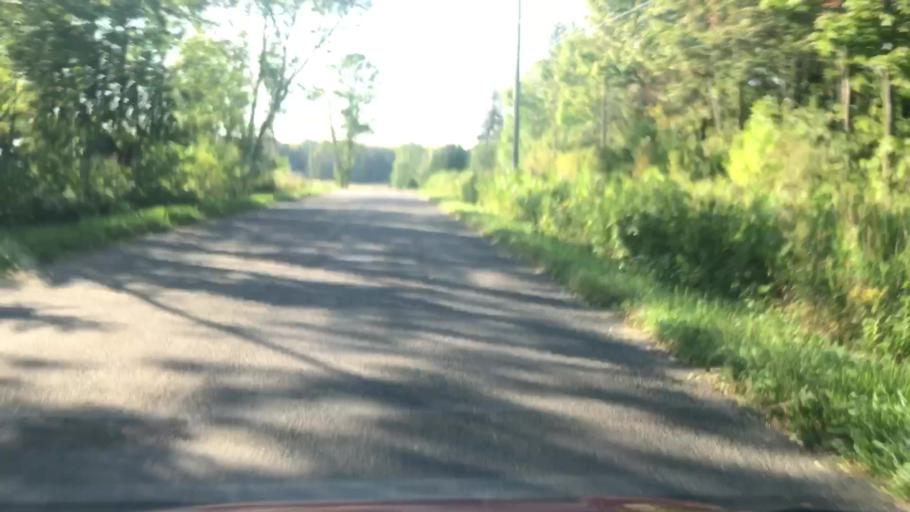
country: US
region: Michigan
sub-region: Chippewa County
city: Sault Ste. Marie
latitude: 46.2932
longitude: -84.0691
